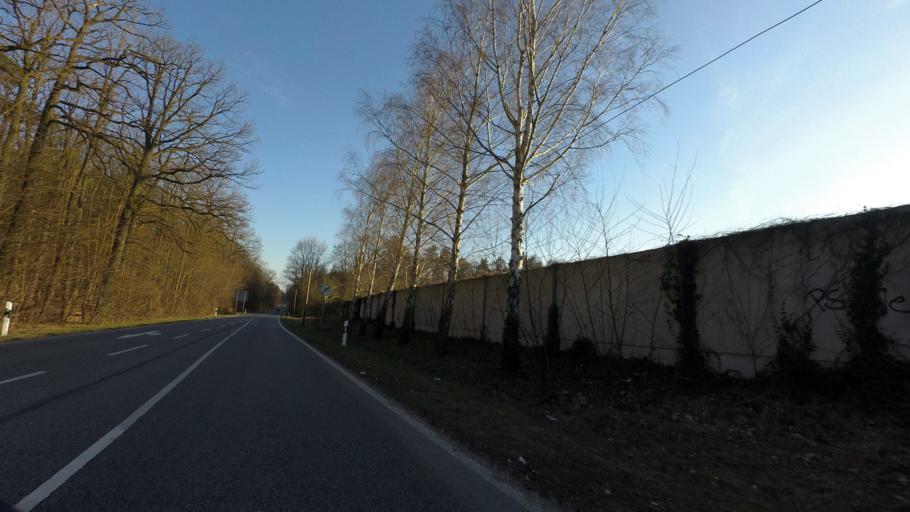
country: DE
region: Brandenburg
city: Eberswalde
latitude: 52.8204
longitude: 13.8319
